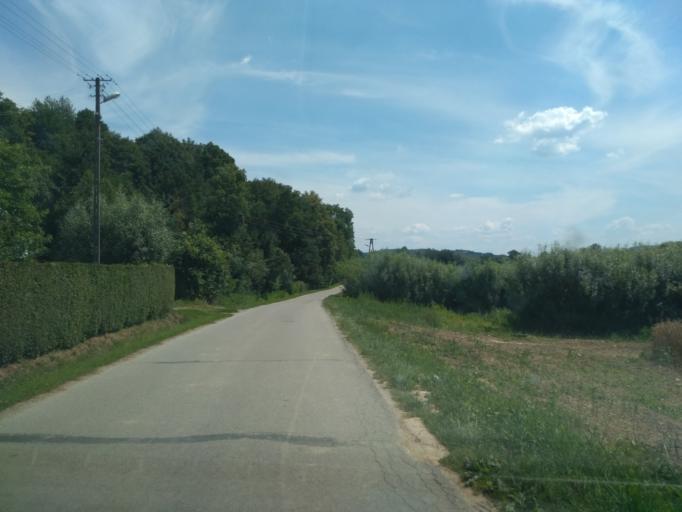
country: PL
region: Subcarpathian Voivodeship
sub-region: Powiat strzyzowski
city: Strzyzow
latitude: 49.8482
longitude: 21.8166
